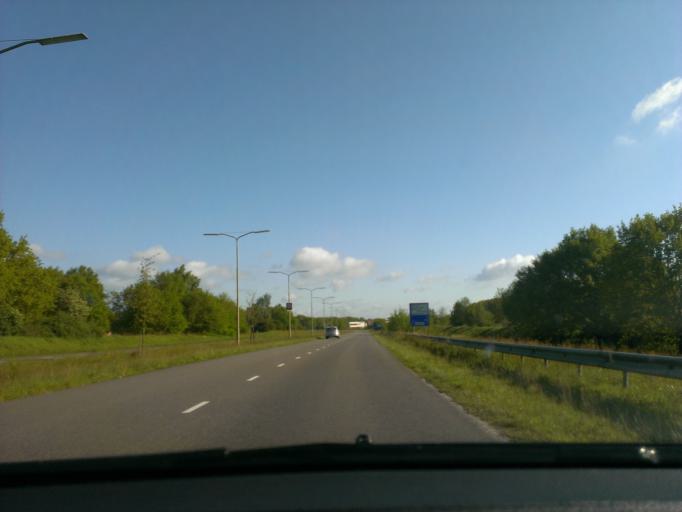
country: NL
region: Drenthe
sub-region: Gemeente Emmen
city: Emmen
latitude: 52.7662
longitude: 6.8964
